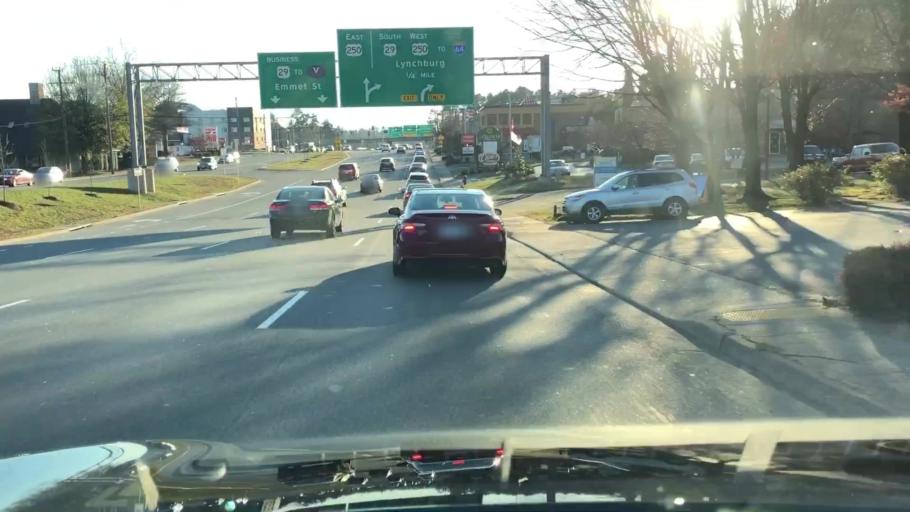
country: US
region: Virginia
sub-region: City of Charlottesville
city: Charlottesville
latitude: 38.0605
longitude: -78.4930
